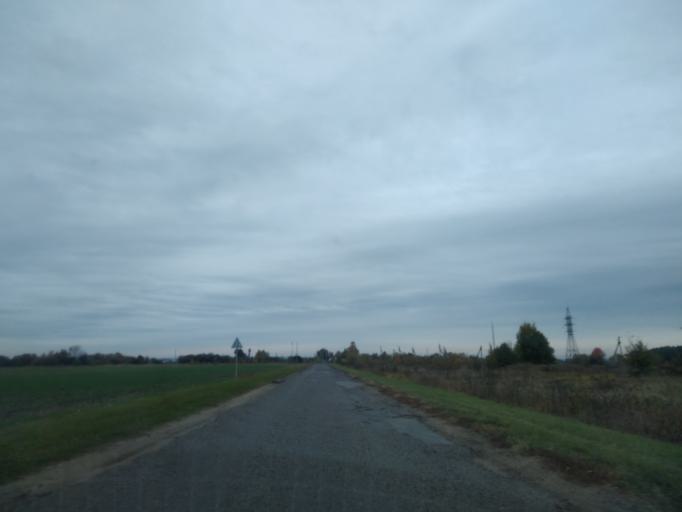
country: RU
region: Lipetsk
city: Zadonsk
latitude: 52.2992
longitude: 38.9343
